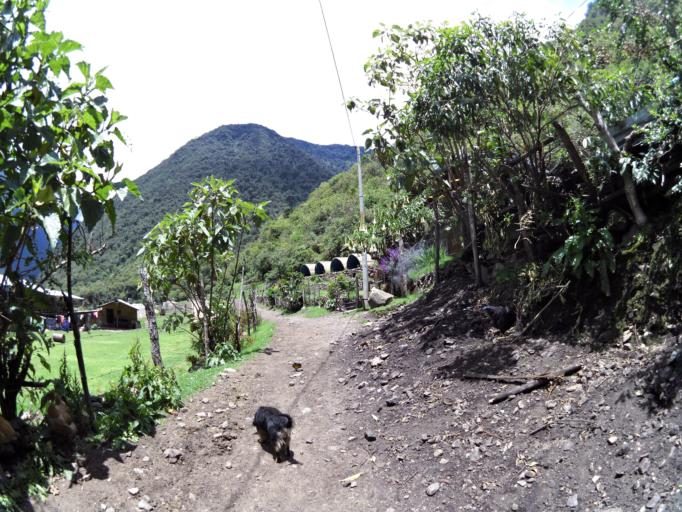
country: PE
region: Cusco
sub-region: Provincia de La Convencion
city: Santa Teresa
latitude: -13.3246
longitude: -72.6646
